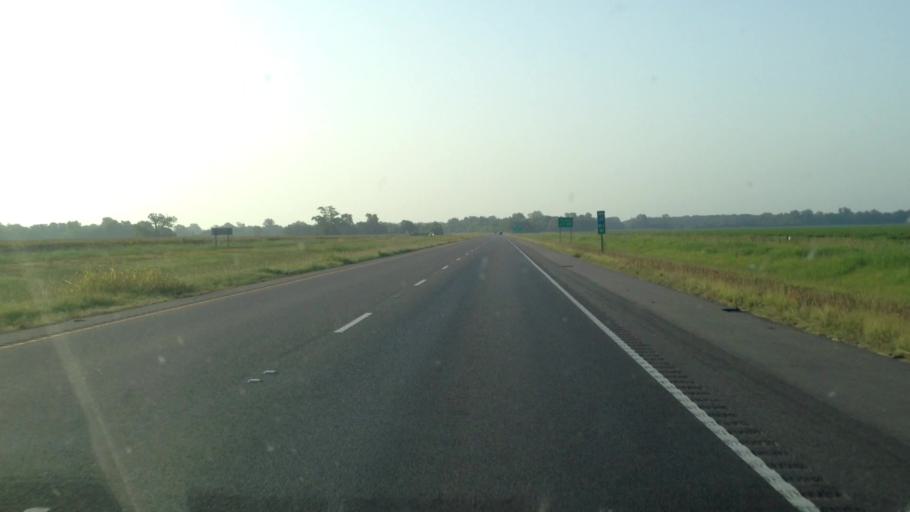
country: US
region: Louisiana
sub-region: Rapides Parish
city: Boyce
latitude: 31.3883
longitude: -92.6872
